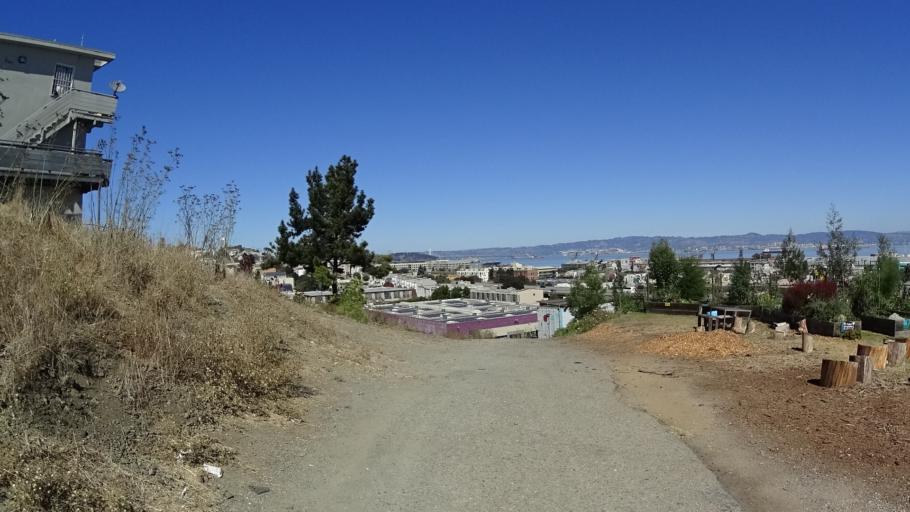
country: US
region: California
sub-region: San Francisco County
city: San Francisco
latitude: 37.7551
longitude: -122.3947
